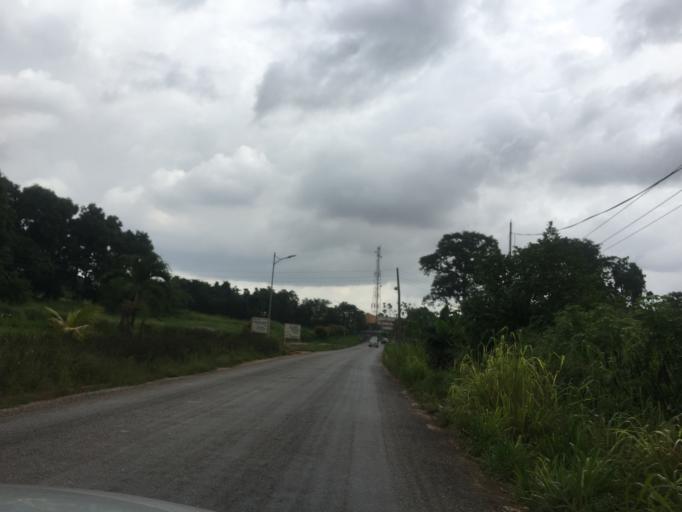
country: GH
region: Ashanti
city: Mamponteng
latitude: 6.6789
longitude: -1.5661
